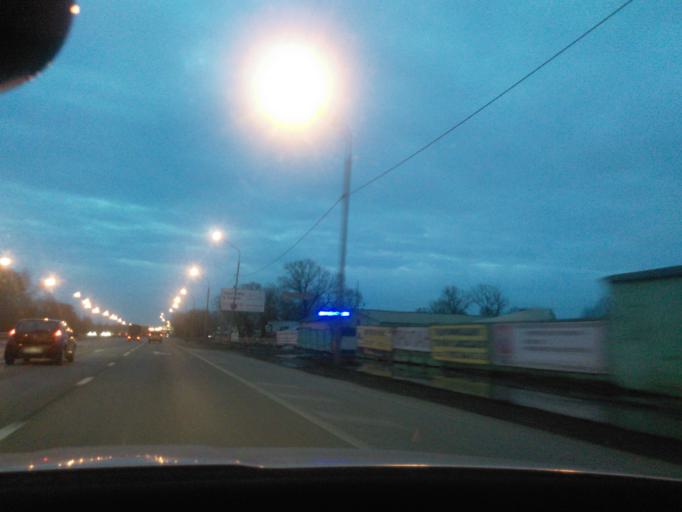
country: RU
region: Moskovskaya
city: Novopodrezkovo
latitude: 55.9449
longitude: 37.3585
